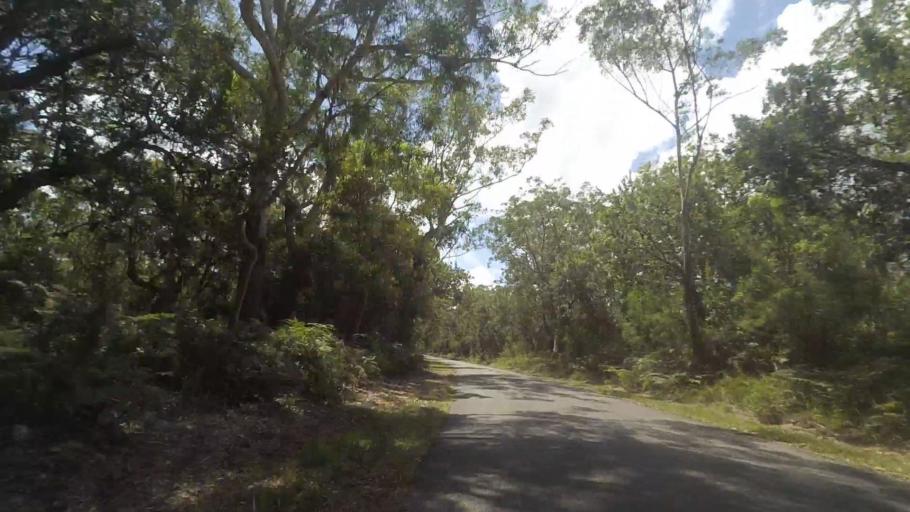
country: AU
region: New South Wales
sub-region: Great Lakes
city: Bulahdelah
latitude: -32.5078
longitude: 152.3172
